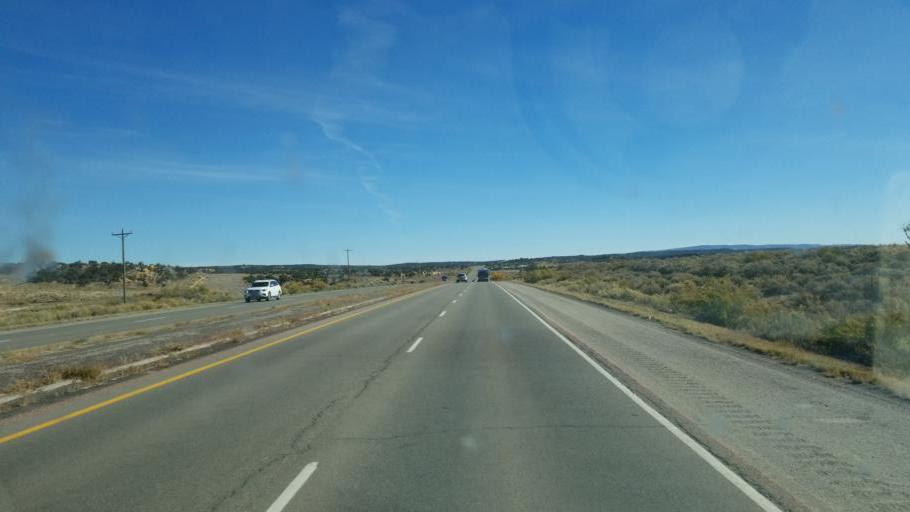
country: US
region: Arizona
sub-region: Apache County
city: Window Rock
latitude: 35.6279
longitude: -108.9298
